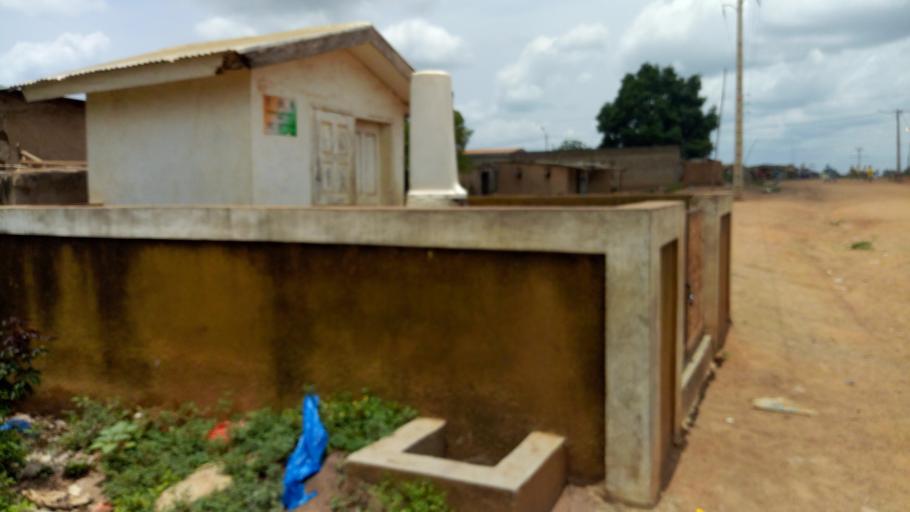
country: CI
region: Vallee du Bandama
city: Bouake
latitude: 7.7024
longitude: -4.9882
